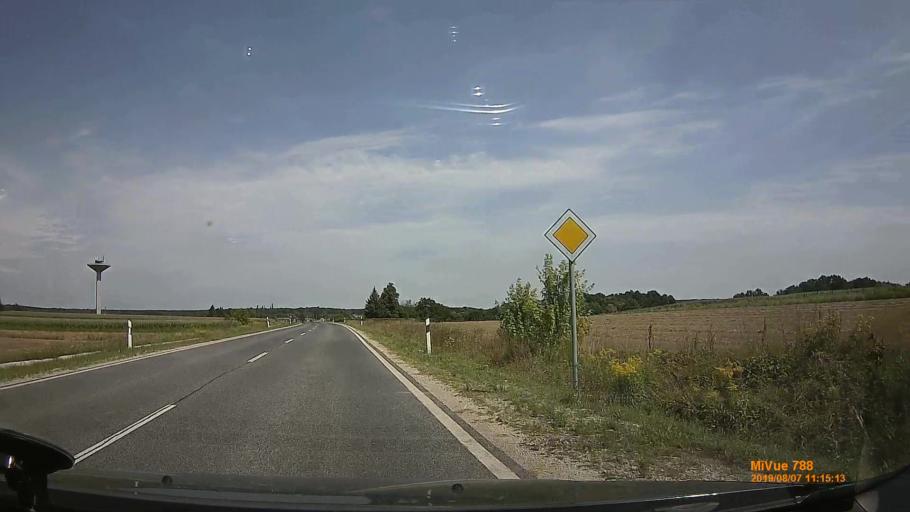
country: HU
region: Zala
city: Lenti
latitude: 46.7134
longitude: 16.5516
